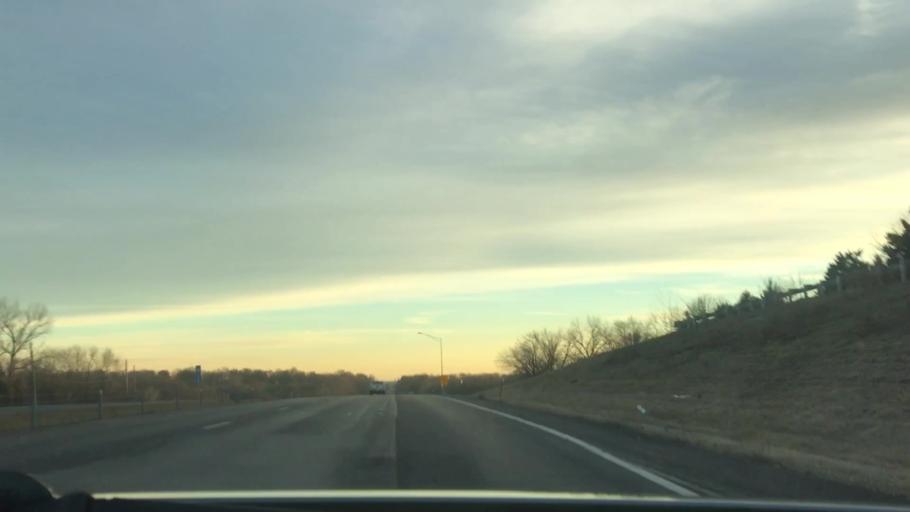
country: US
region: Missouri
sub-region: Clay County
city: Gladstone
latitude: 39.2218
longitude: -94.5895
